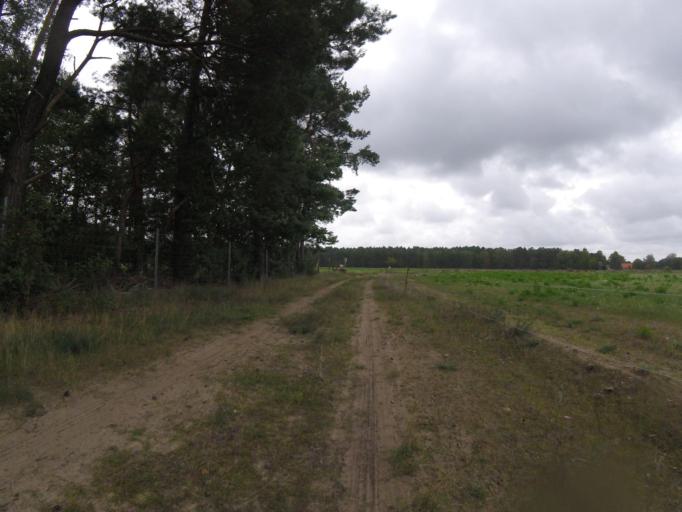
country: DE
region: Brandenburg
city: Gross Koris
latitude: 52.1816
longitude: 13.6735
